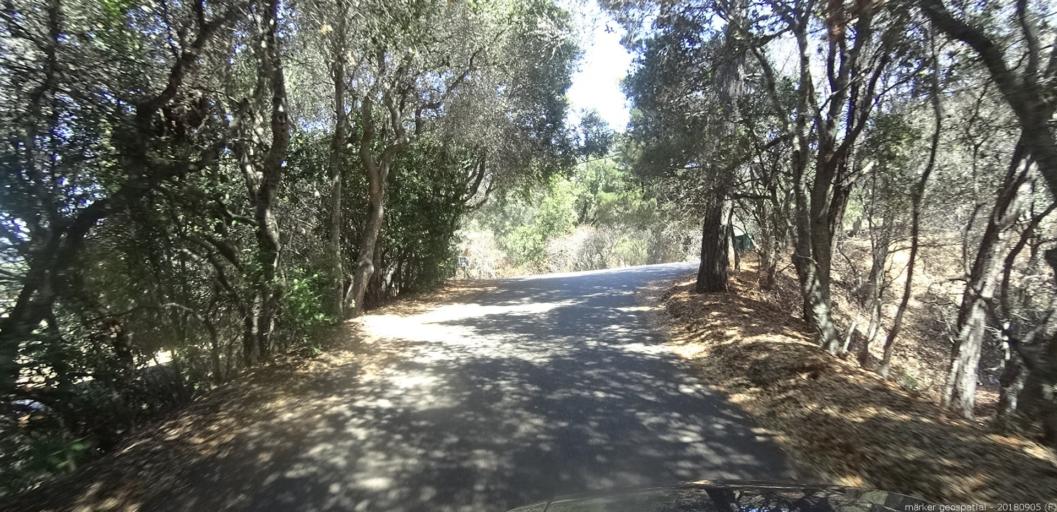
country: US
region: California
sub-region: Monterey County
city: Carmel Valley Village
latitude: 36.5013
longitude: -121.7577
